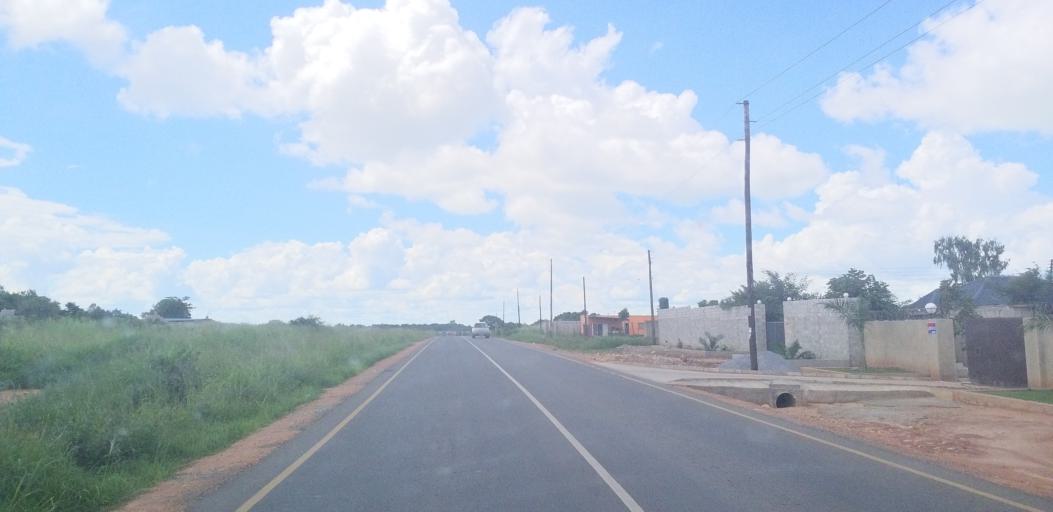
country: ZM
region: Lusaka
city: Lusaka
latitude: -15.3277
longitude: 28.3281
